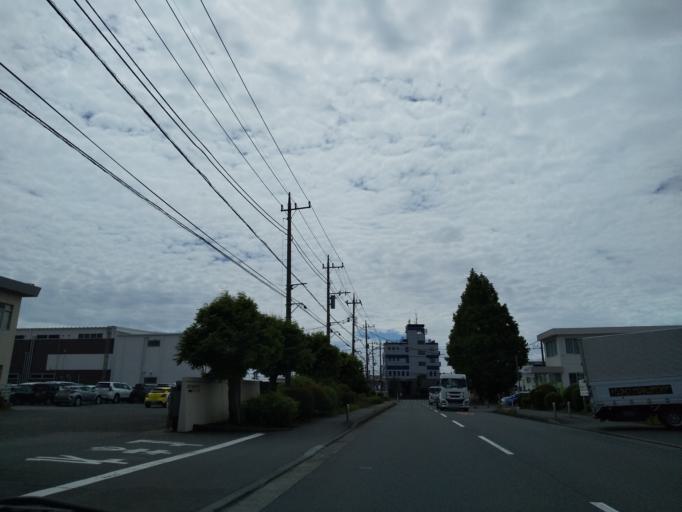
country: JP
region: Kanagawa
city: Zama
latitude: 35.5111
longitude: 139.3547
